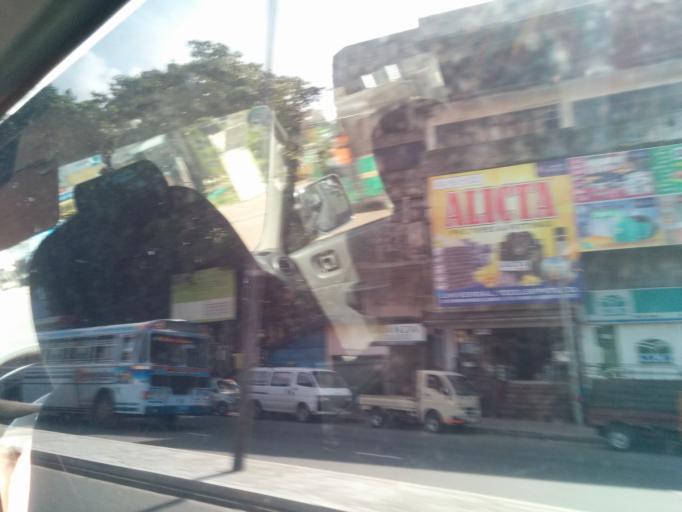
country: LK
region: Western
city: Colombo
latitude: 6.9392
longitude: 79.8661
